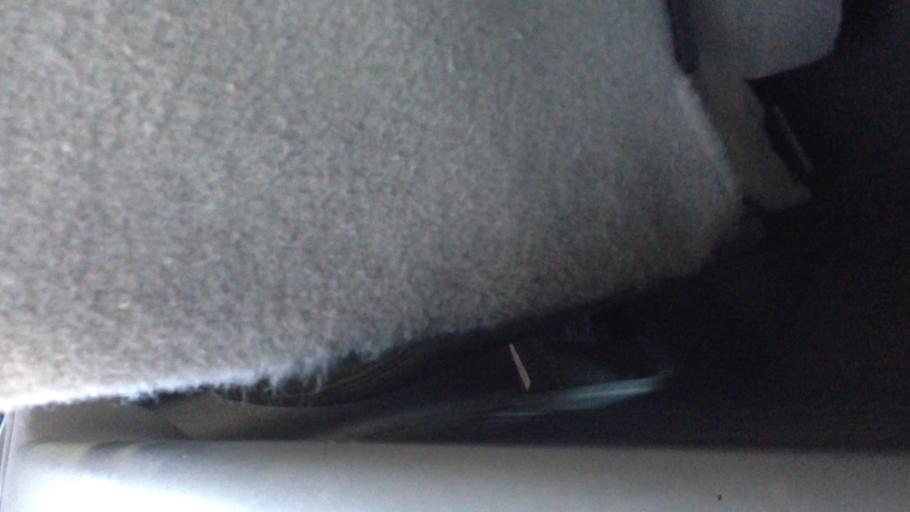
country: US
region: New York
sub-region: Columbia County
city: Oakdale
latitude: 42.2361
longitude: -73.7819
